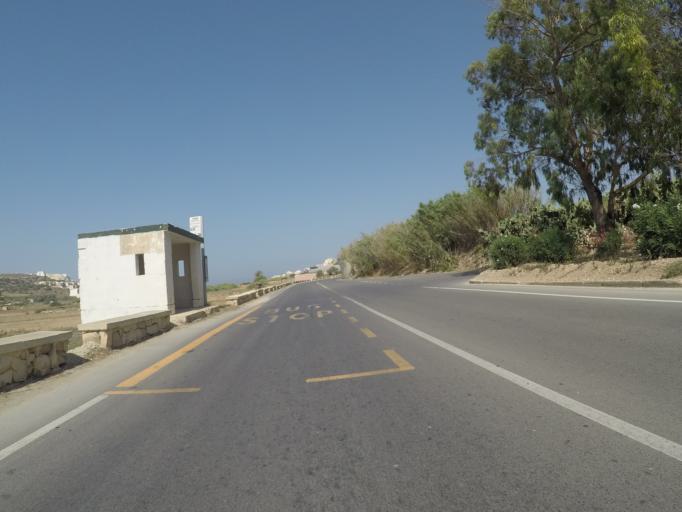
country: MT
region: Il-Mellieha
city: Mellieha
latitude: 35.9409
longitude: 14.3761
